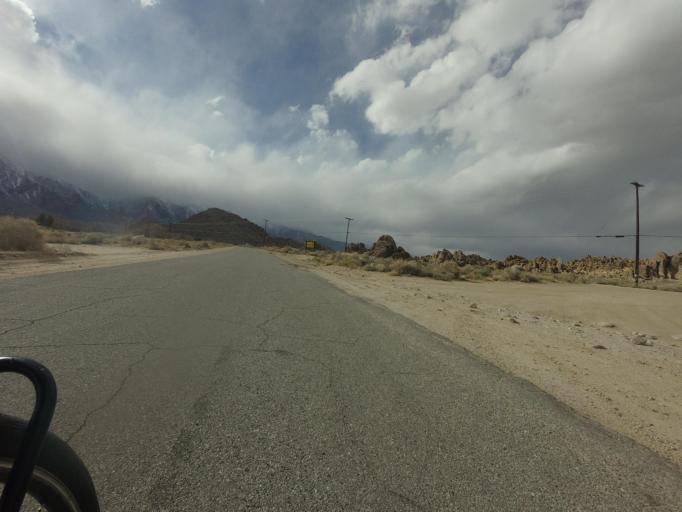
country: US
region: California
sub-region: Inyo County
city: Lone Pine
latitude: 36.5971
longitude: -118.1113
